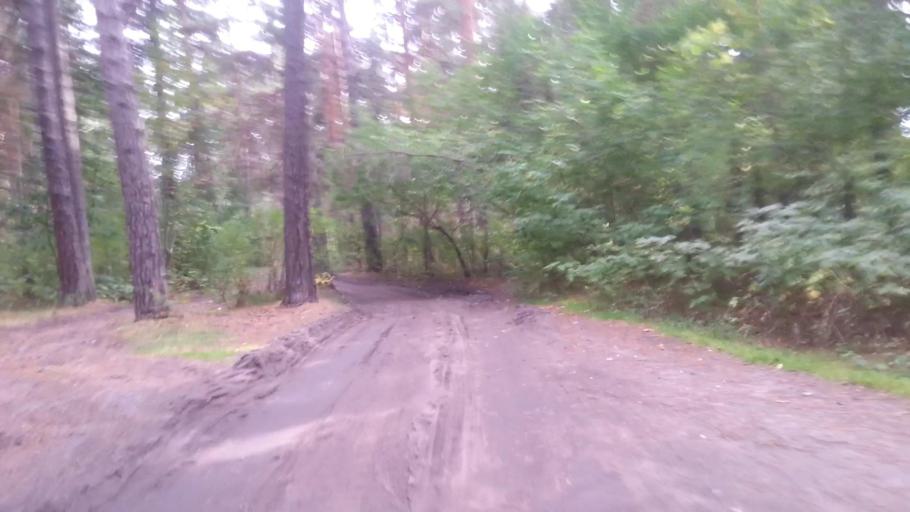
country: RU
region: Altai Krai
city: Yuzhnyy
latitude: 53.3096
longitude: 83.6987
